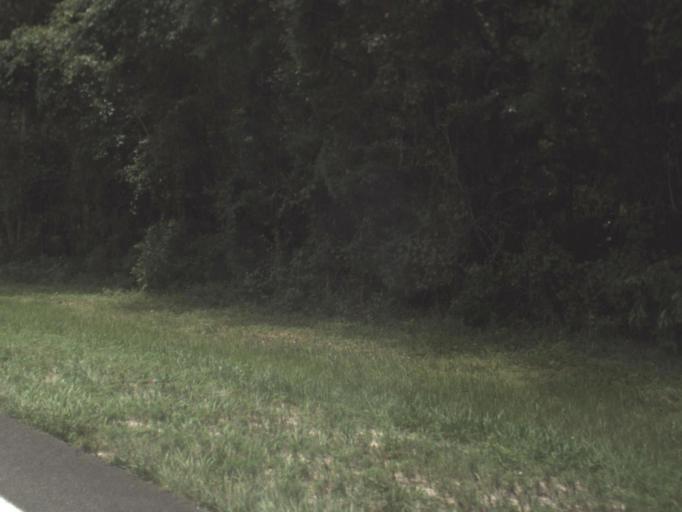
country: US
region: Florida
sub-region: Alachua County
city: Archer
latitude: 29.4846
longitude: -82.4904
